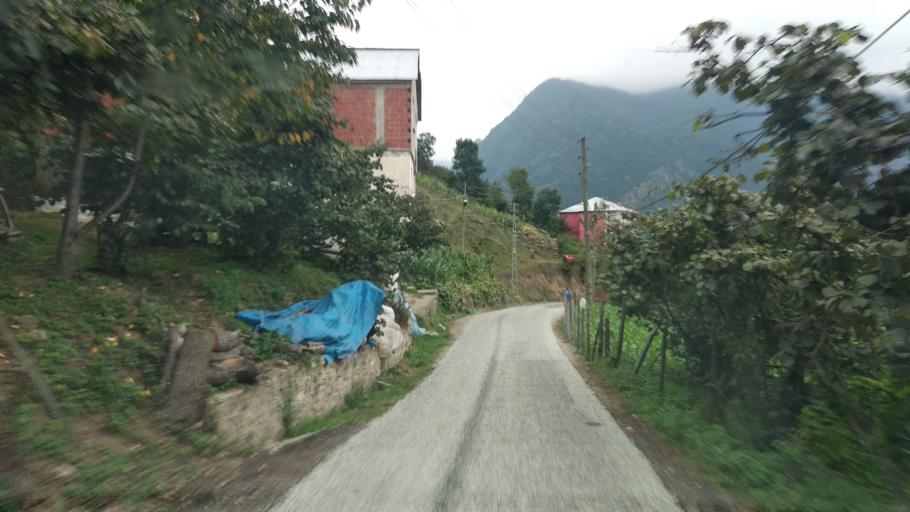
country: TR
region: Giresun
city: Dogankent
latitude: 40.7449
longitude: 38.9910
